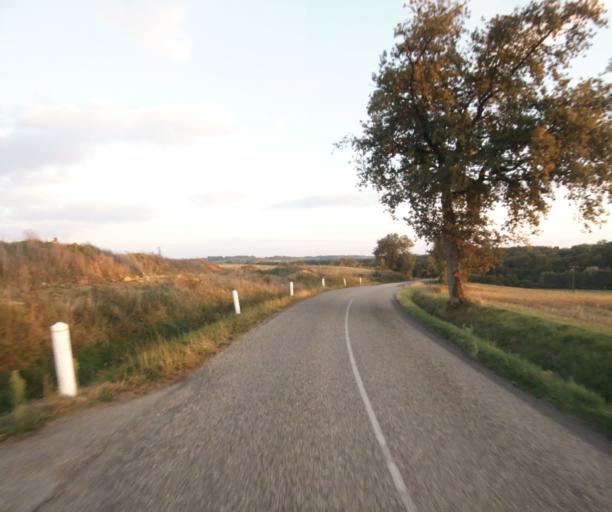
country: FR
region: Midi-Pyrenees
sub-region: Departement du Gers
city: Vic-Fezensac
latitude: 43.7962
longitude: 0.2467
